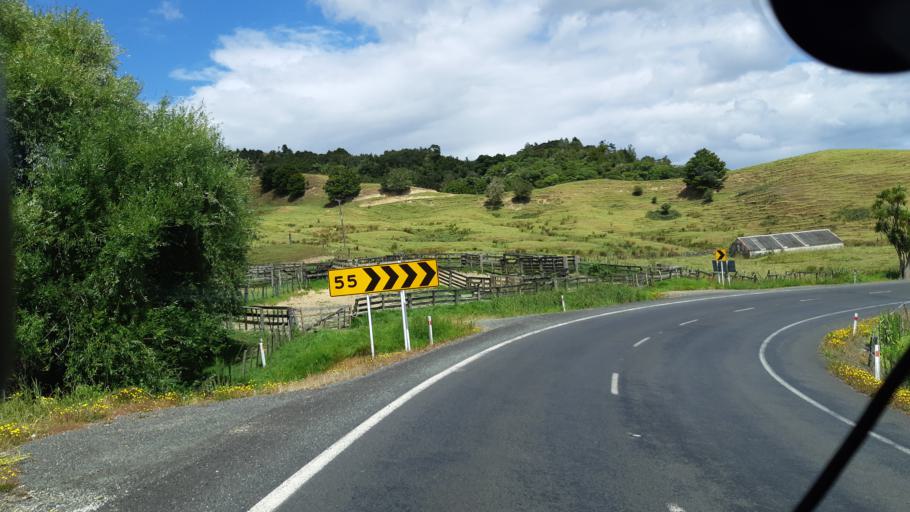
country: NZ
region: Northland
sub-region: Far North District
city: Taipa
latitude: -35.2459
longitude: 173.5469
